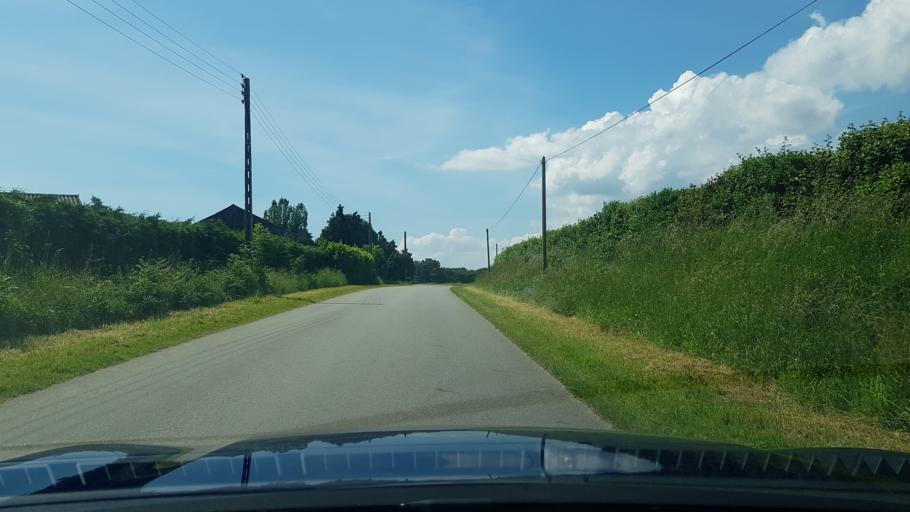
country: FR
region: Brittany
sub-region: Departement du Finistere
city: Clohars-Carnoet
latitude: 47.7878
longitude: -3.5574
